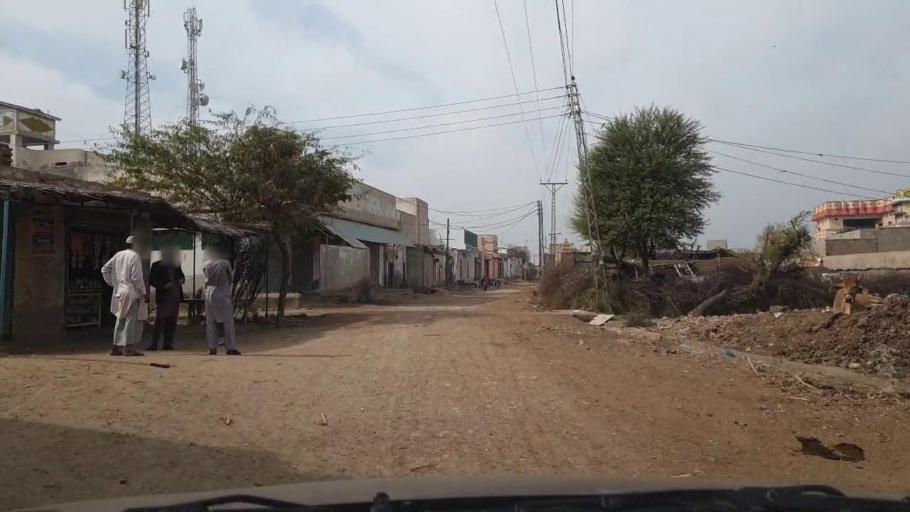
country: PK
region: Sindh
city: Sinjhoro
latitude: 26.0989
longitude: 68.8609
